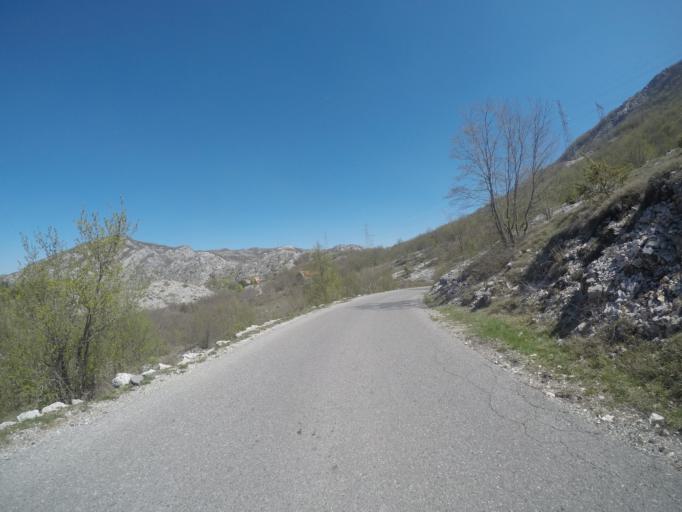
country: ME
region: Cetinje
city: Cetinje
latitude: 42.4539
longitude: 18.8733
